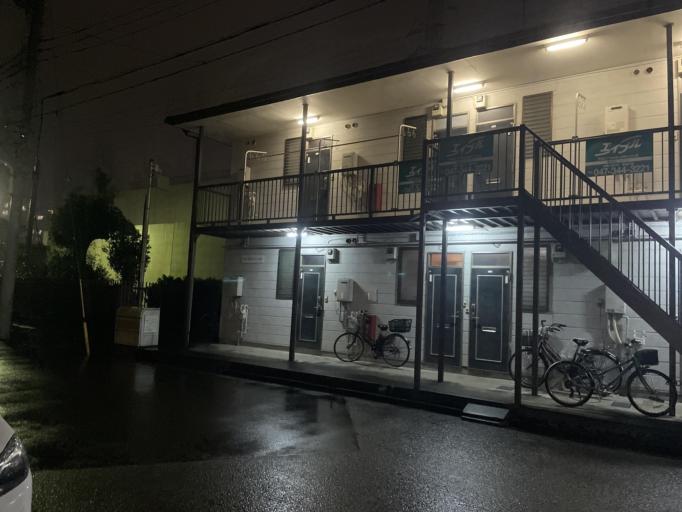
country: JP
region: Chiba
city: Nagareyama
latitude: 35.8260
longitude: 139.9087
